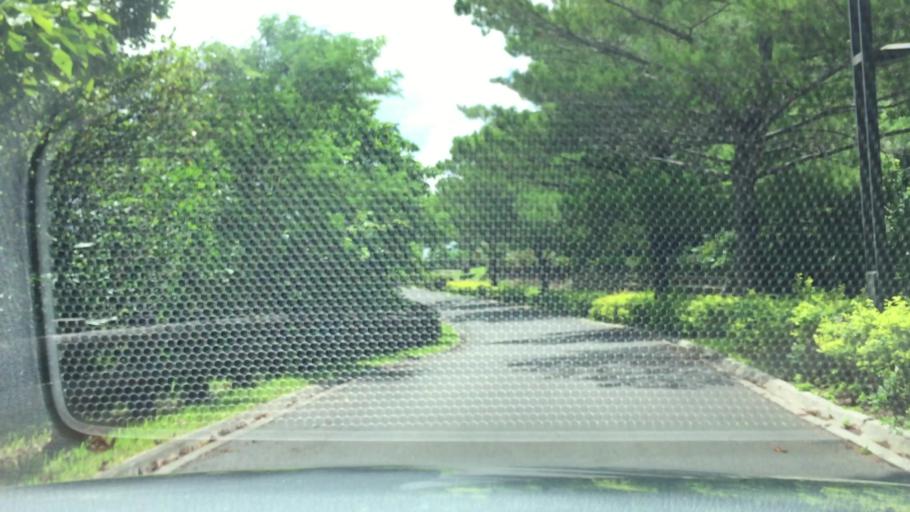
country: JP
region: Okinawa
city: Ishigaki
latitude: 24.3855
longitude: 124.1731
